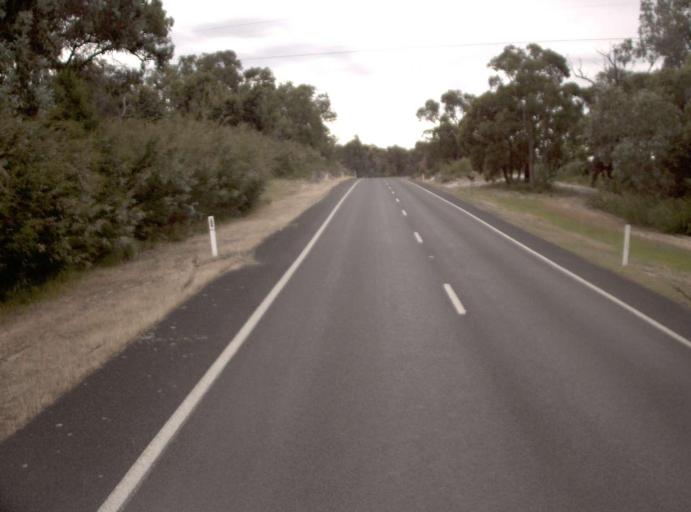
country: AU
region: Victoria
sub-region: Wellington
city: Sale
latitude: -38.3432
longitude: 147.0040
